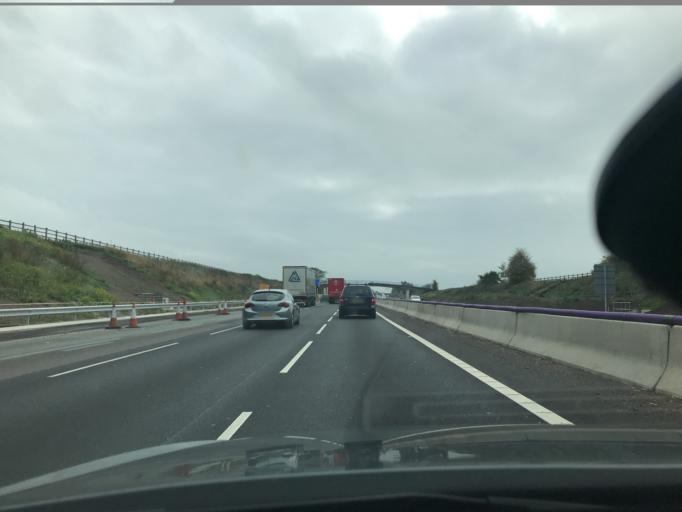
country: GB
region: England
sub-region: Cheshire East
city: Holmes Chapel
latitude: 53.1814
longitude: -2.3683
